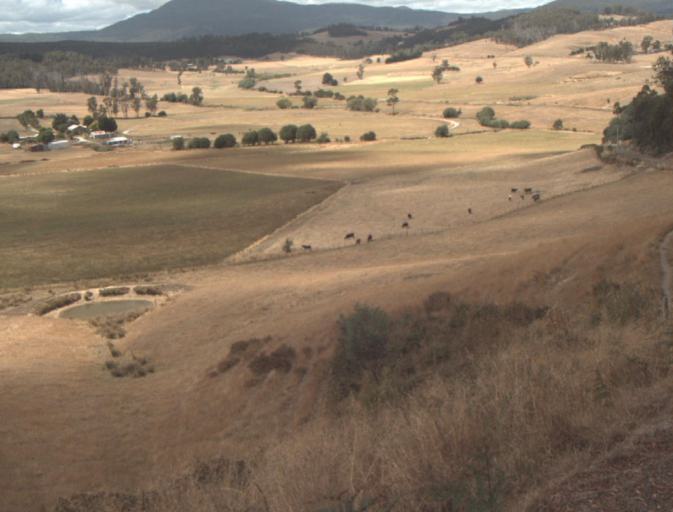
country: AU
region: Tasmania
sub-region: Launceston
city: Mayfield
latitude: -41.2076
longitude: 147.1397
